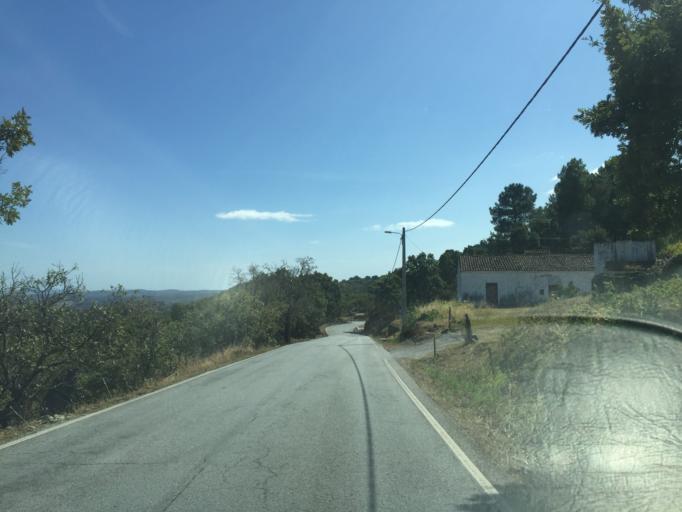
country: PT
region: Portalegre
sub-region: Marvao
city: Marvao
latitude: 39.4015
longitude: -7.3764
